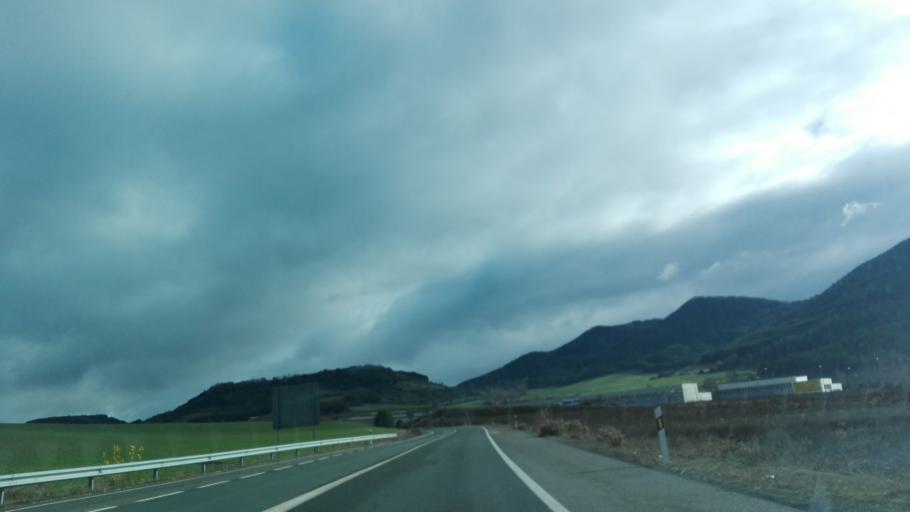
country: ES
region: Navarre
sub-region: Provincia de Navarra
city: Egues-Uharte
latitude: 42.8243
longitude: -1.5575
